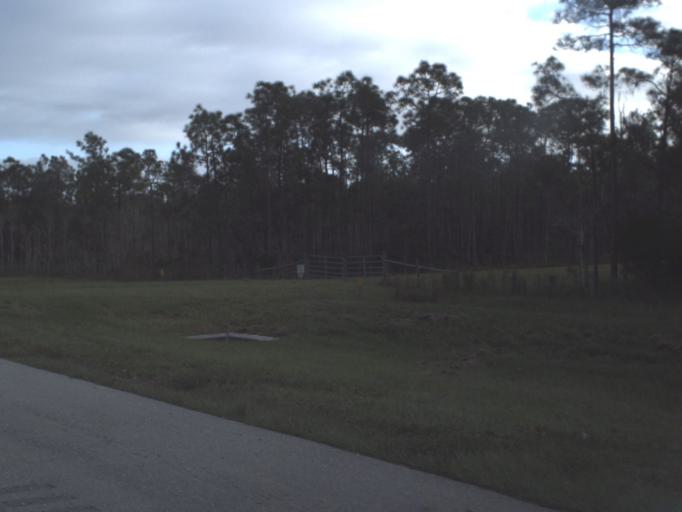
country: US
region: Florida
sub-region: Lee County
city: Bonita Springs
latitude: 26.3925
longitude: -81.7723
